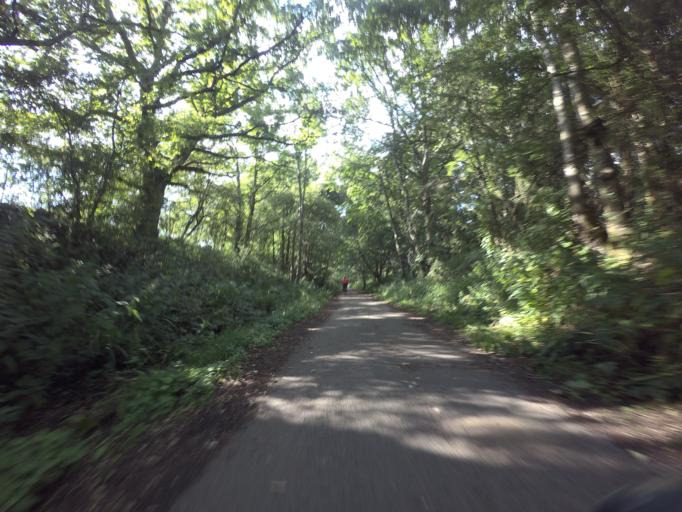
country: GB
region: England
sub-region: East Sussex
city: Horam
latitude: 50.9217
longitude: 0.2544
